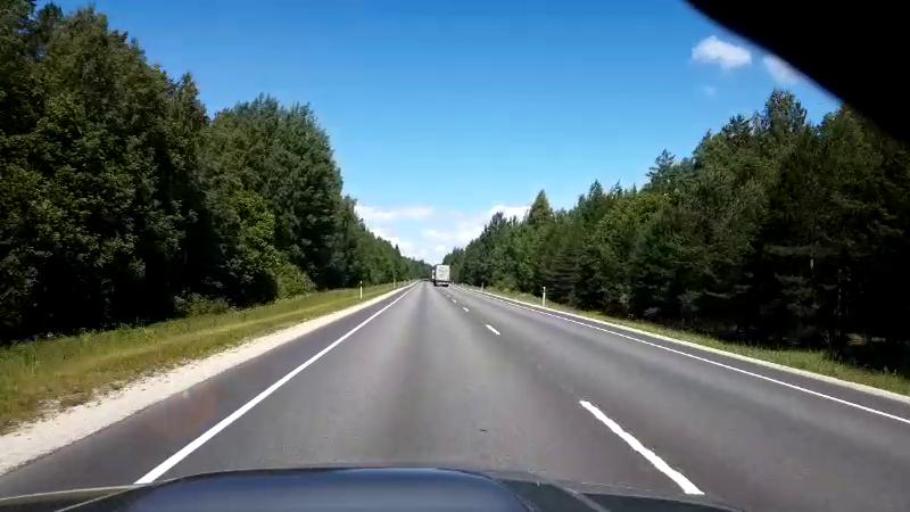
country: LV
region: Salacgrivas
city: Ainazi
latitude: 58.1004
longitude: 24.5081
